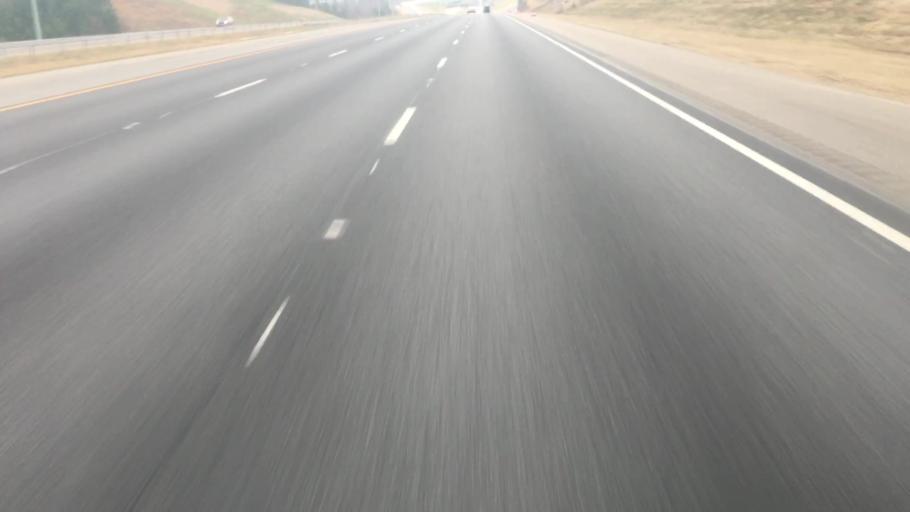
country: US
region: Alabama
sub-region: Jefferson County
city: Fultondale
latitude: 33.5825
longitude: -86.8283
